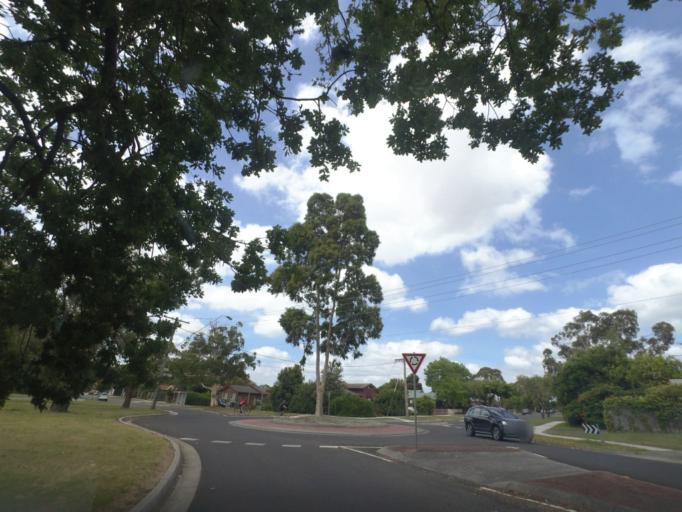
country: AU
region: Victoria
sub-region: Maroondah
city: Croydon South
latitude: -37.8046
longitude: 145.2838
